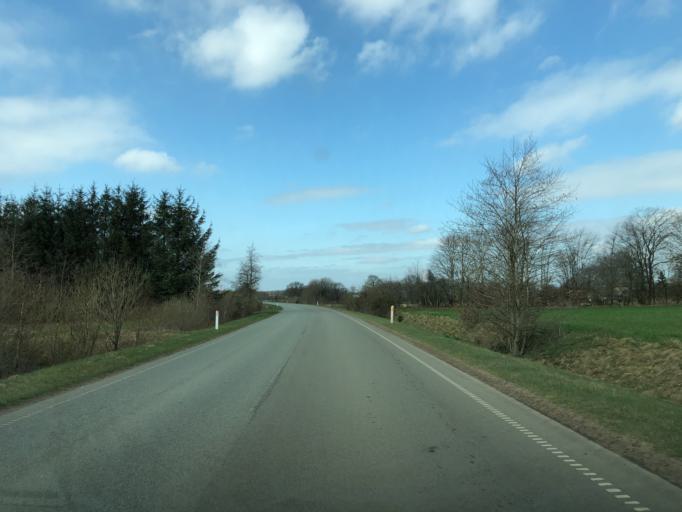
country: DK
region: Central Jutland
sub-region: Ikast-Brande Kommune
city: Brande
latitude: 55.9284
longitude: 9.1771
